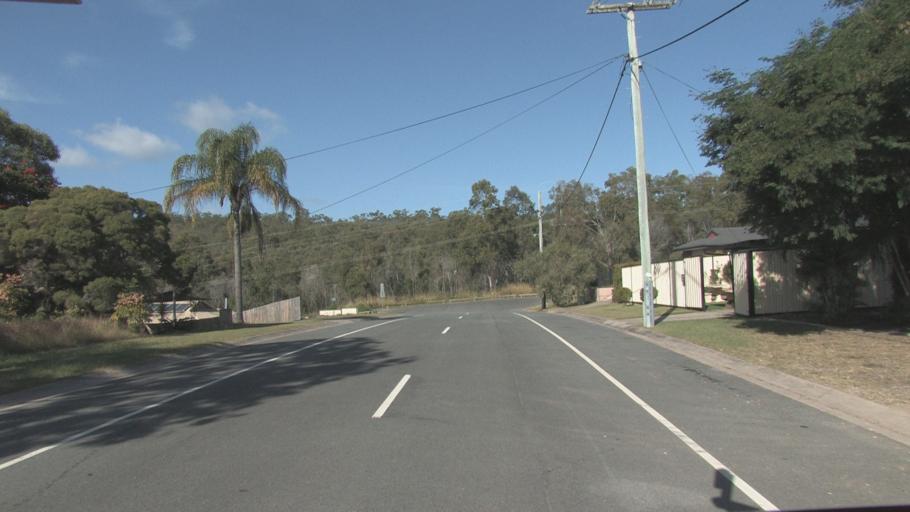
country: AU
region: Queensland
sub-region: Logan
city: Windaroo
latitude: -27.7238
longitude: 153.1810
